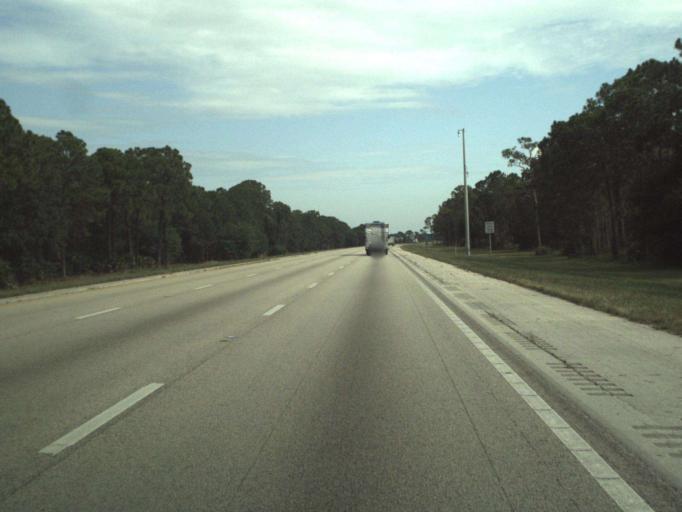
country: US
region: Florida
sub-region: Martin County
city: Palm City
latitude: 27.1719
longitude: -80.3936
